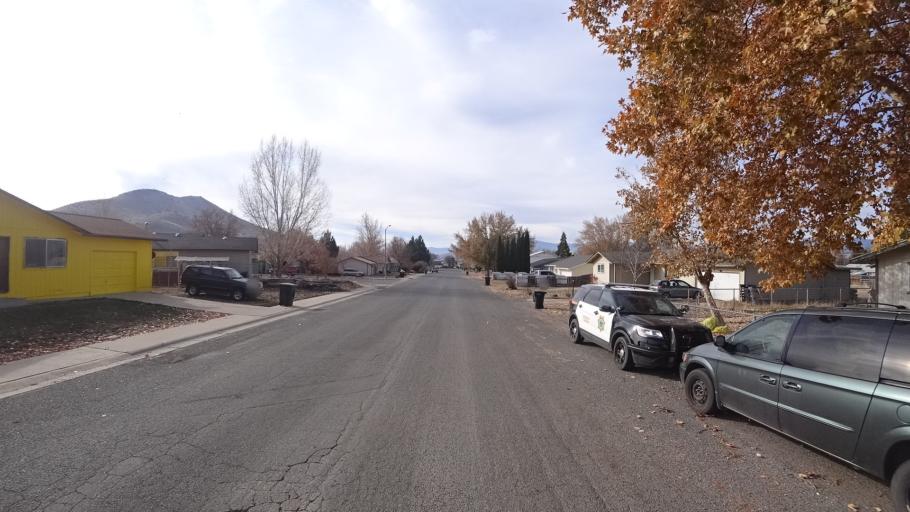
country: US
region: California
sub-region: Siskiyou County
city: Montague
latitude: 41.7269
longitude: -122.5181
